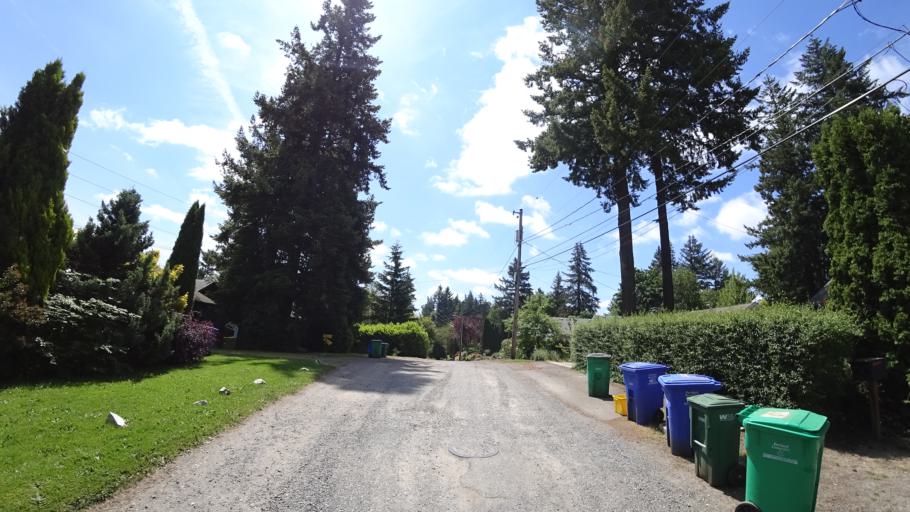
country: US
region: Oregon
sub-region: Washington County
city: Garden Home-Whitford
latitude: 45.4627
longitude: -122.7193
